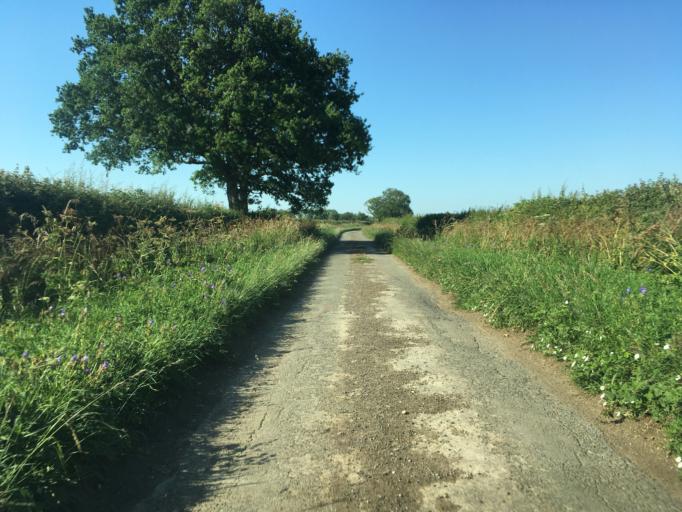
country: GB
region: England
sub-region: South Gloucestershire
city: Chipping Sodbury
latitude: 51.5146
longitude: -2.4004
